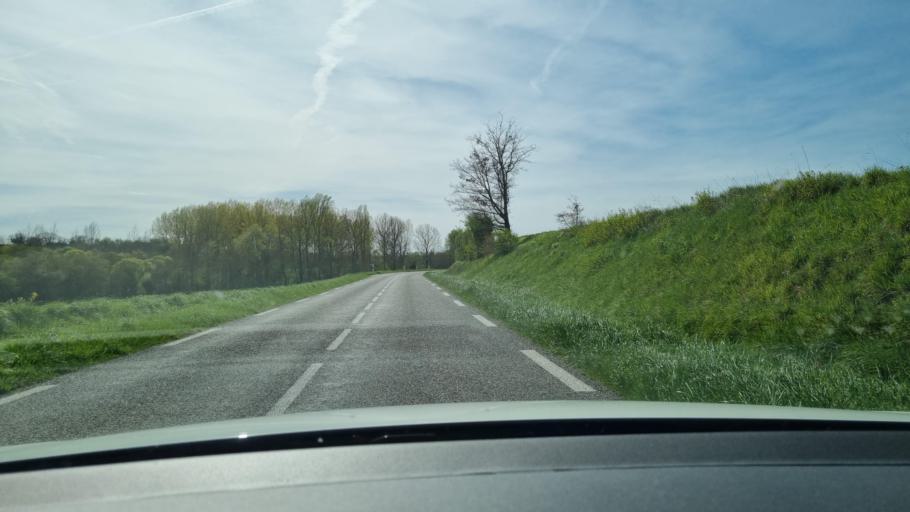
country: FR
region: Midi-Pyrenees
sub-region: Departement du Gers
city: Samatan
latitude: 43.4890
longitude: 0.9876
